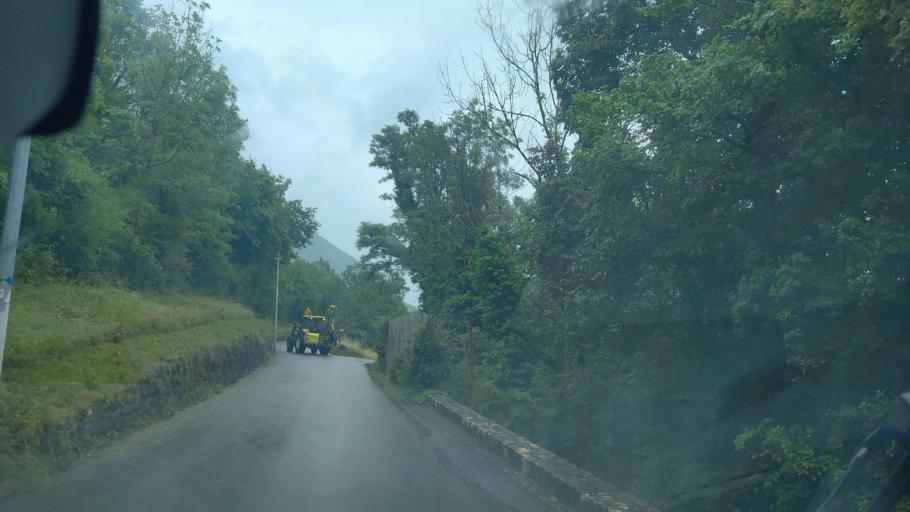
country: FR
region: Rhone-Alpes
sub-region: Departement de la Savoie
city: Chatillon
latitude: 45.8073
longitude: 5.8568
